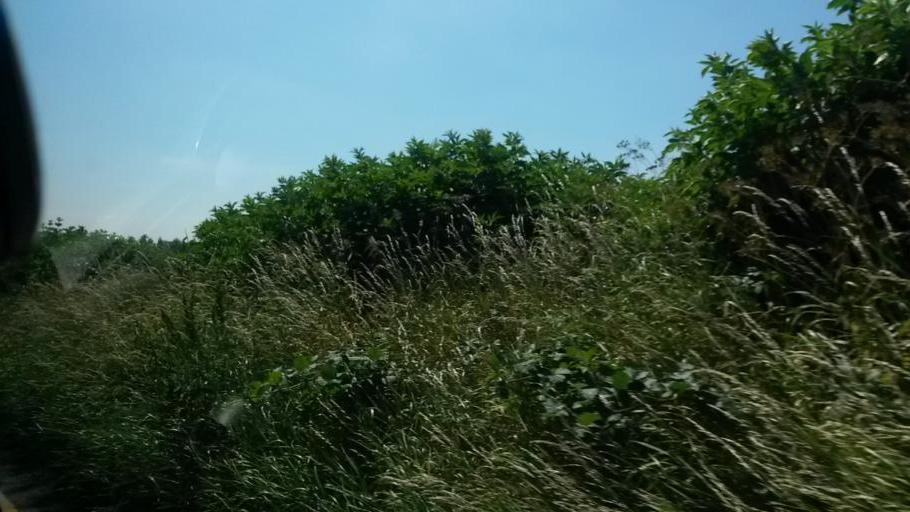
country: IE
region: Leinster
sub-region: An Mhi
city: Stamullin
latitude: 53.5683
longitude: -6.3155
